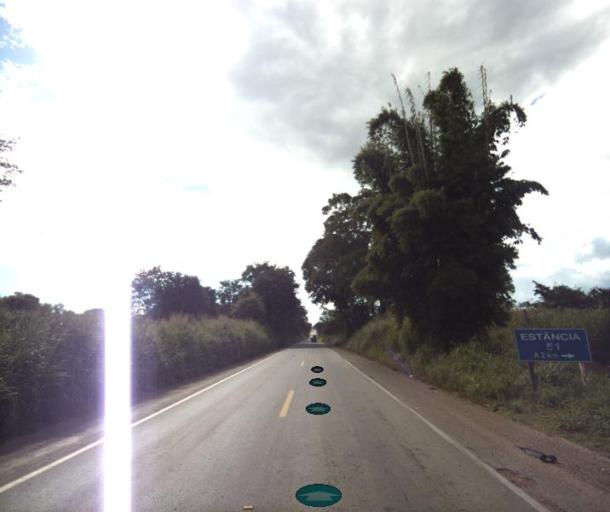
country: BR
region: Goias
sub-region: Jaragua
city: Jaragua
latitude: -15.6754
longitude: -49.3458
